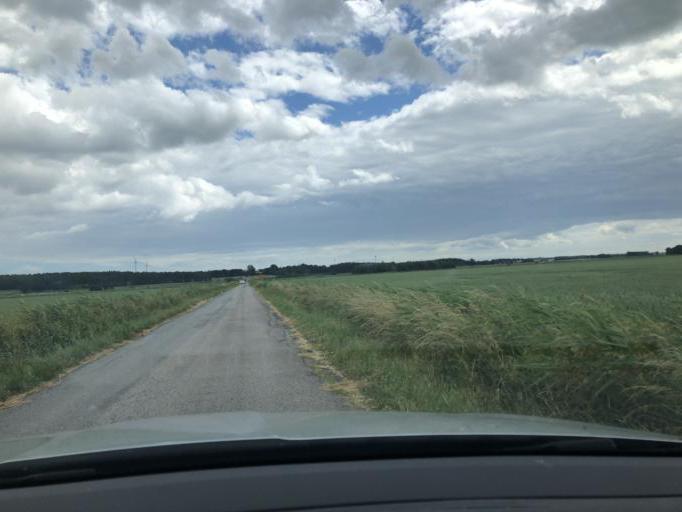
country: SE
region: Blekinge
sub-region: Solvesborgs Kommun
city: Soelvesborg
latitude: 56.0982
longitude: 14.6311
